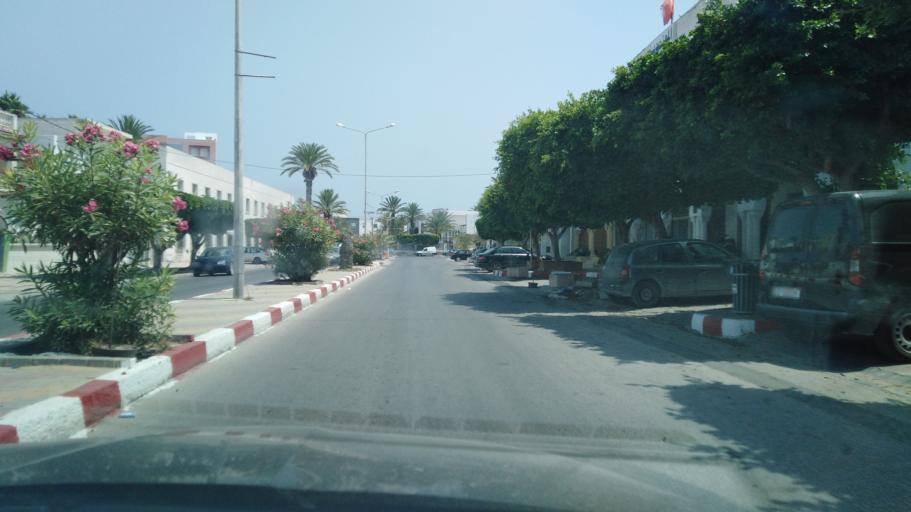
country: TN
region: Al Mahdiyah
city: Mahdia
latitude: 35.5066
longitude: 11.0546
